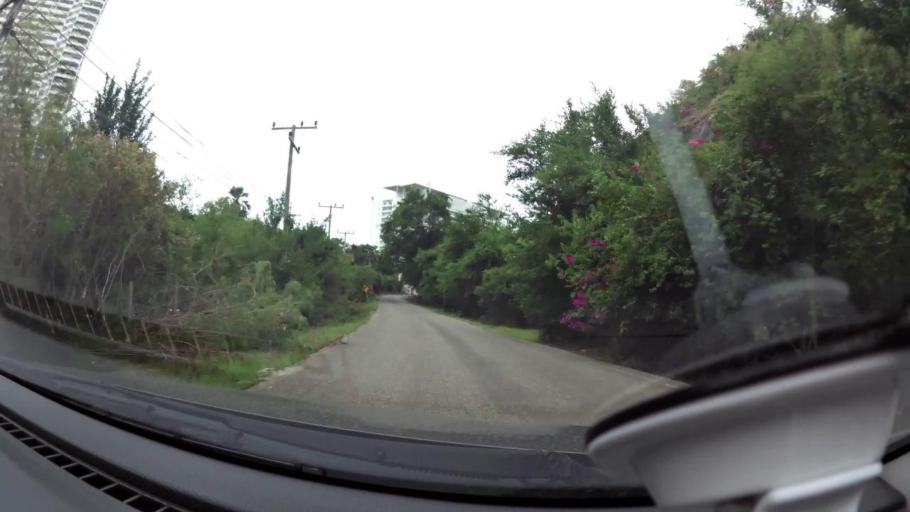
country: TH
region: Prachuap Khiri Khan
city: Pran Buri
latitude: 12.4326
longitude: 99.9779
